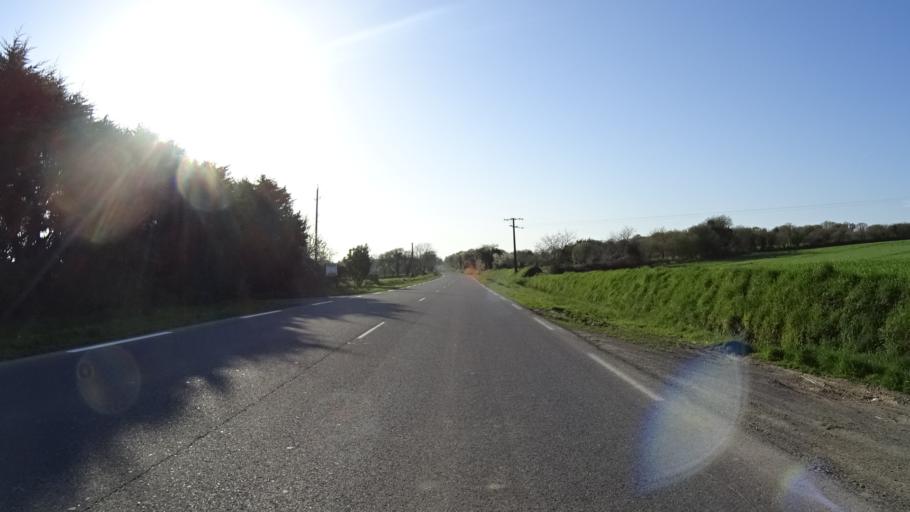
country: FR
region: Brittany
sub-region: Departement du Finistere
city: La Roche-Maurice
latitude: 48.4332
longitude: -4.1521
